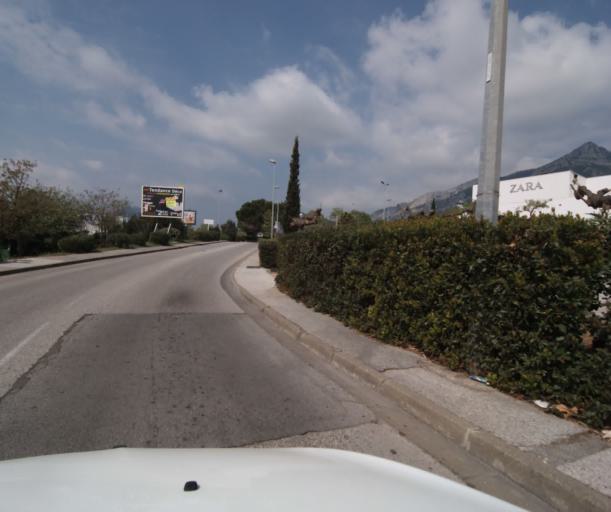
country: FR
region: Provence-Alpes-Cote d'Azur
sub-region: Departement du Var
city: La Garde
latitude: 43.1398
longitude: 6.0187
